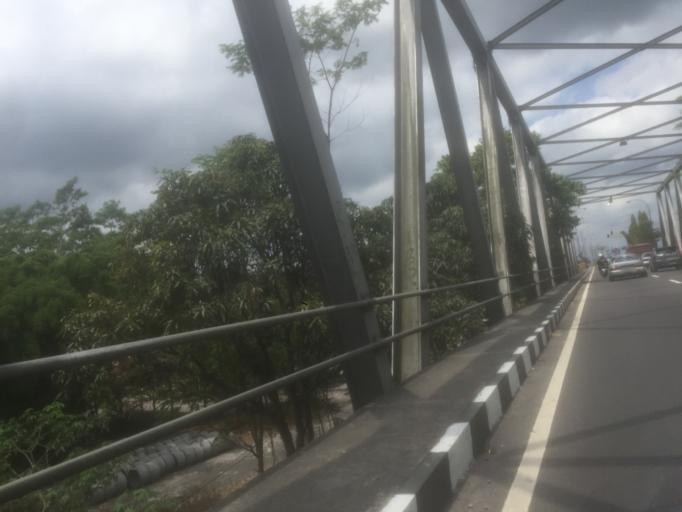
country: ID
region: Central Java
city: Muntilan
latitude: -7.6446
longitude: 110.3238
